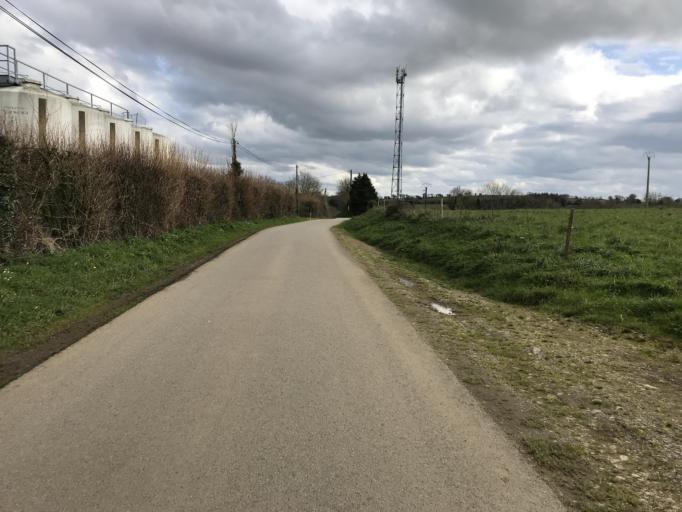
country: FR
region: Brittany
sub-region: Departement du Finistere
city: Hopital-Camfrout
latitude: 48.3181
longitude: -4.2138
